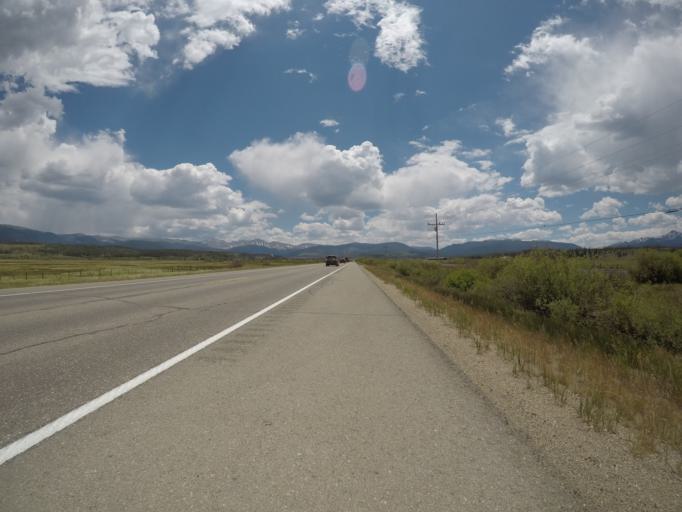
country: US
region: Colorado
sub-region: Grand County
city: Fraser
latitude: 39.9683
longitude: -105.8243
